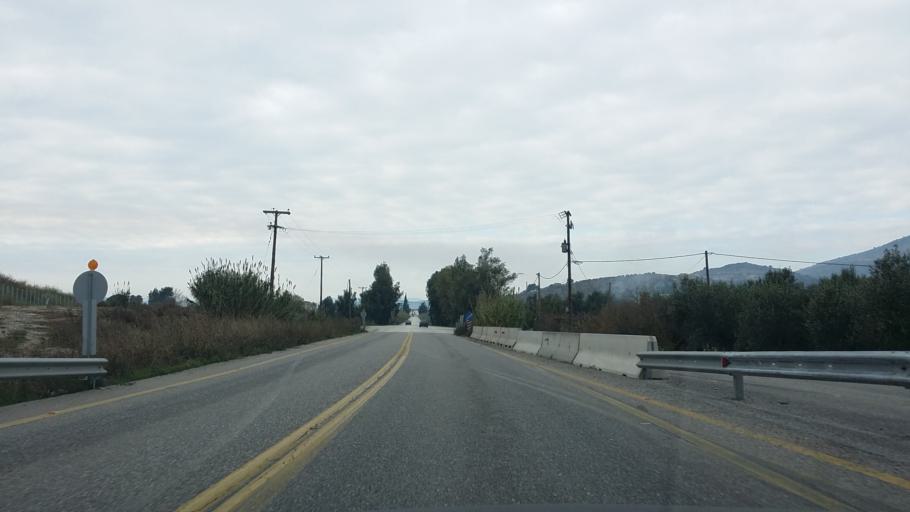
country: GR
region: West Greece
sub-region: Nomos Aitolias kai Akarnanias
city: Mesolongi
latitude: 38.3936
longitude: 21.4282
